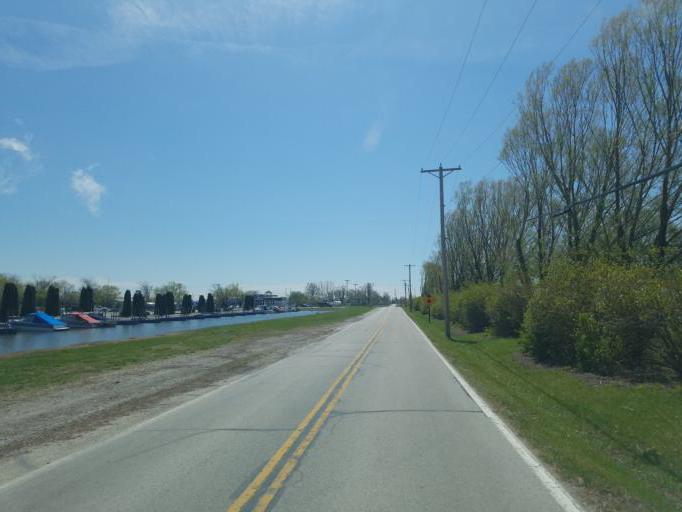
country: US
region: Ohio
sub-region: Ottawa County
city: Oak Harbor
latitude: 41.6065
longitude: -83.1070
